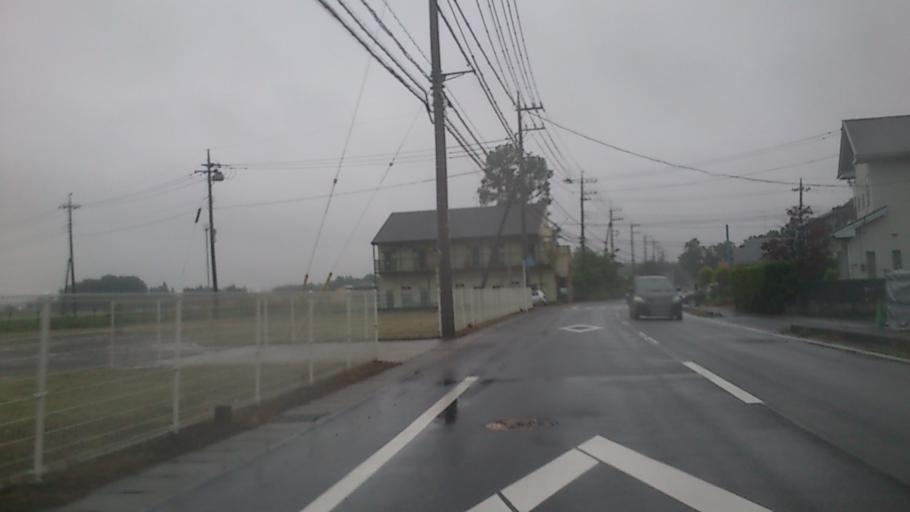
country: JP
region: Tochigi
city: Otawara
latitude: 36.9148
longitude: 139.9775
